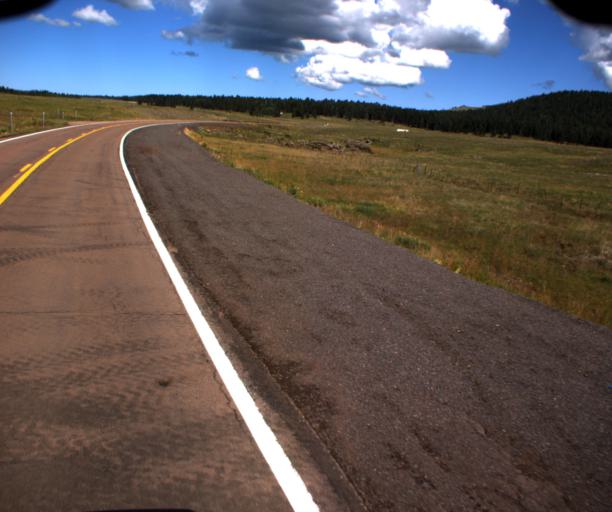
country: US
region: Arizona
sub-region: Apache County
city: Eagar
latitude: 34.0505
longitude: -109.5407
